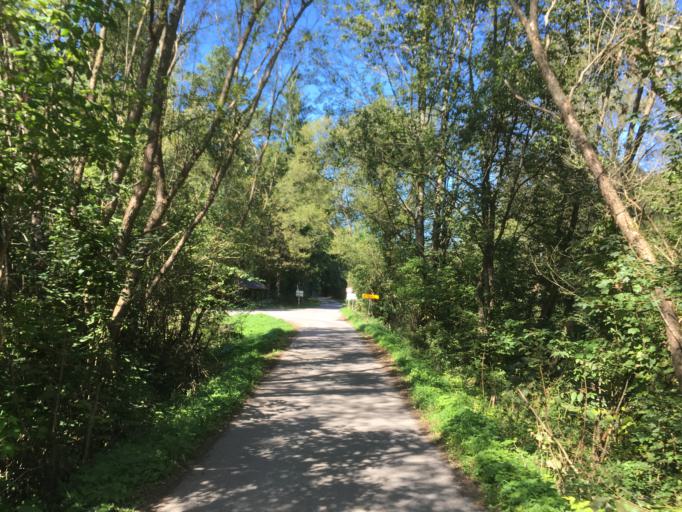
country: SK
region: Trenciansky
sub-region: Okres Povazska Bystrica
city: Povazska Bystrica
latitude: 49.0178
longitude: 18.4402
